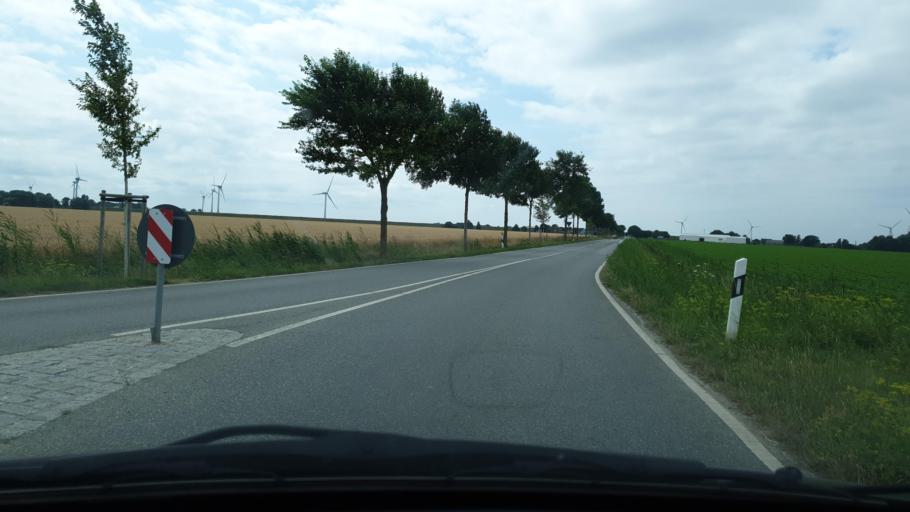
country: DE
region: Schleswig-Holstein
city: Kronprinzenkoog
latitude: 53.9484
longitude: 8.9590
